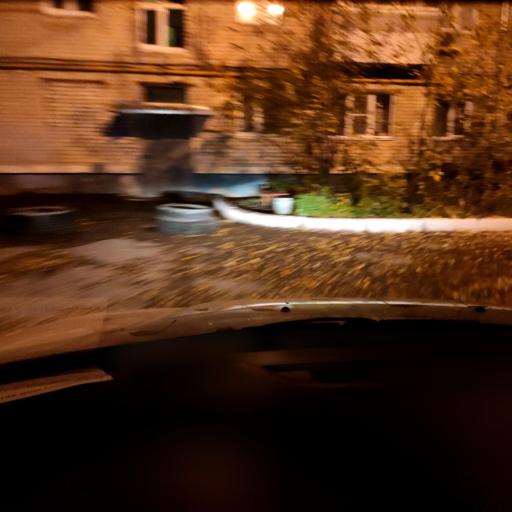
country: RU
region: Samara
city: Tol'yatti
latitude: 53.5167
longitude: 49.4160
